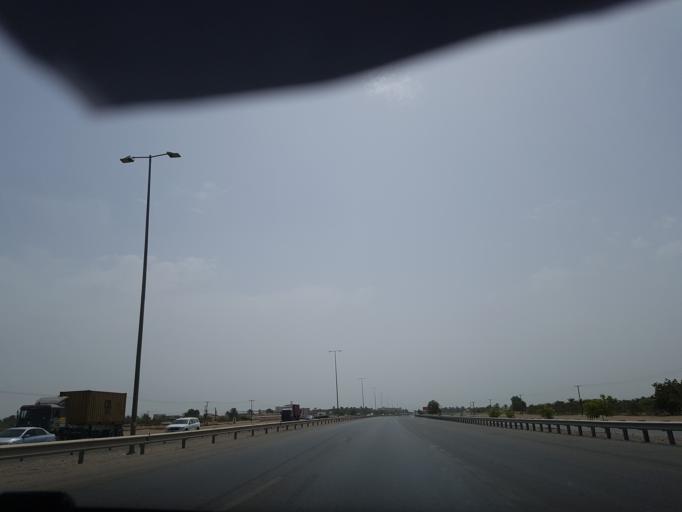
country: OM
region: Al Batinah
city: Barka'
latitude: 23.7263
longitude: 57.7213
